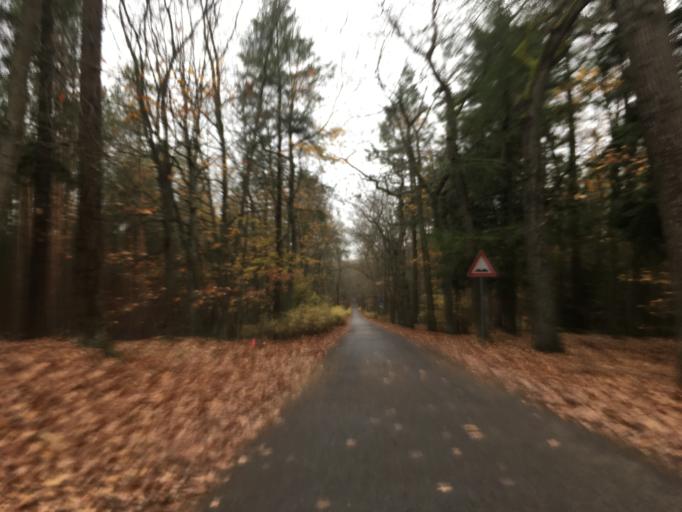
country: DE
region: Brandenburg
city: Mixdorf
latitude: 52.1680
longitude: 14.4450
